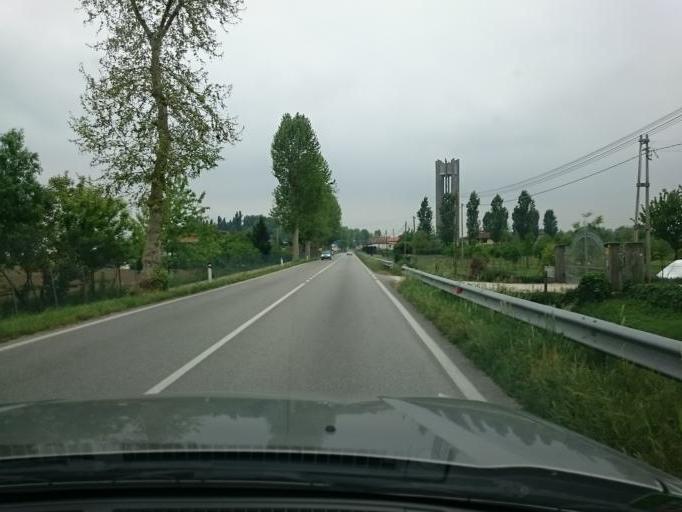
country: IT
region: Veneto
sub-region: Provincia di Padova
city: Cartura
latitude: 45.2906
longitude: 11.8700
